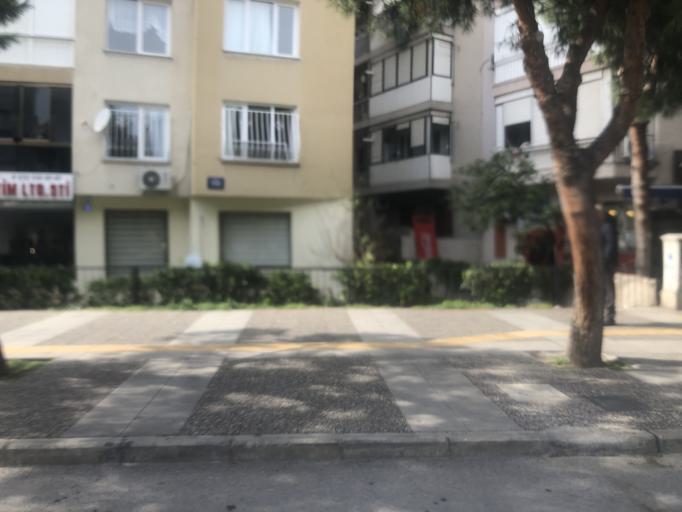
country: TR
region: Izmir
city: Karsiyaka
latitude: 38.4541
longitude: 27.1061
